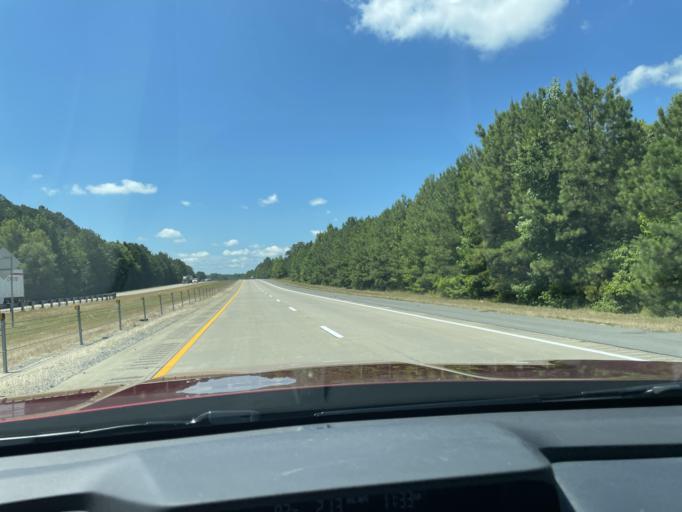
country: US
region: Arkansas
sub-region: Jefferson County
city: Redfield
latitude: 34.4886
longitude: -92.2087
